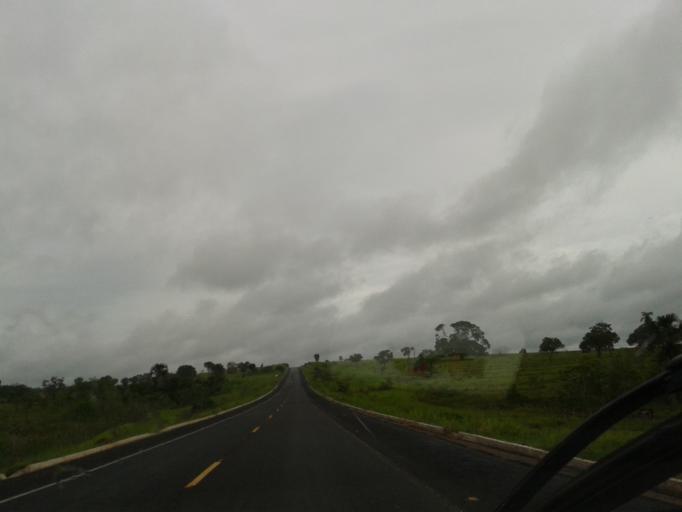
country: BR
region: Minas Gerais
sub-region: Santa Vitoria
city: Santa Vitoria
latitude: -19.2661
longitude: -50.0067
